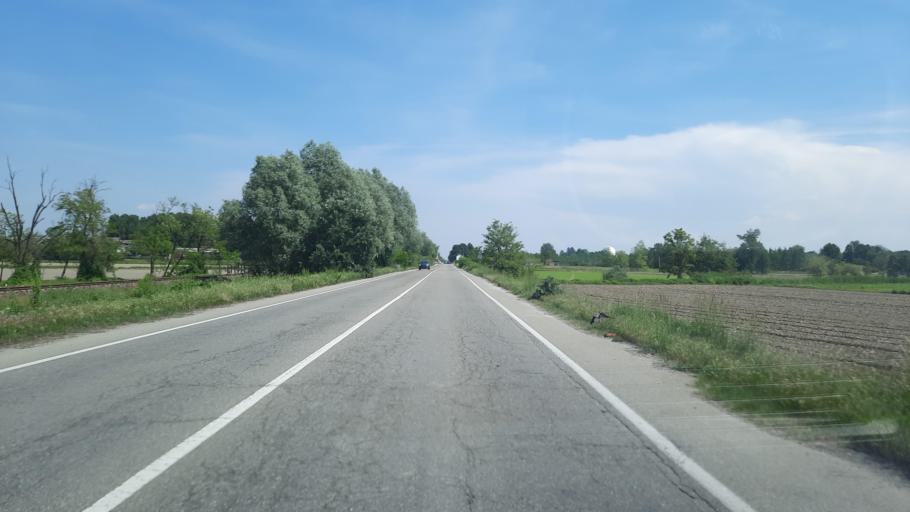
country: IT
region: Lombardy
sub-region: Provincia di Pavia
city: Cergnago
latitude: 45.2368
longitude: 8.7939
